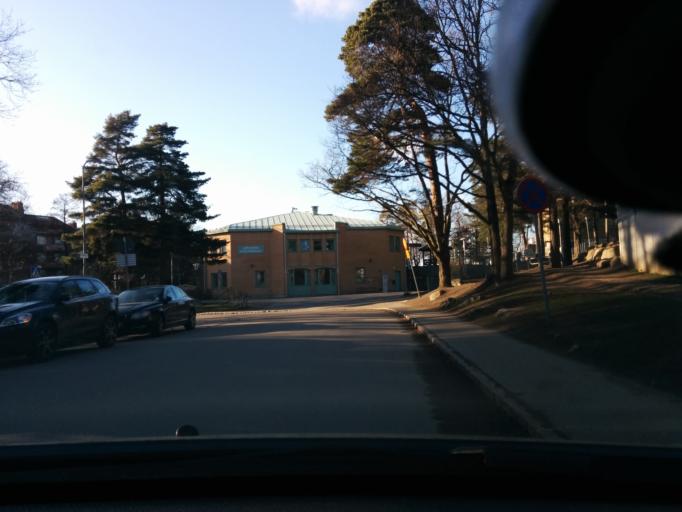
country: SE
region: Stockholm
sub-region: Solna Kommun
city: Solna
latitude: 59.3089
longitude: 17.9970
